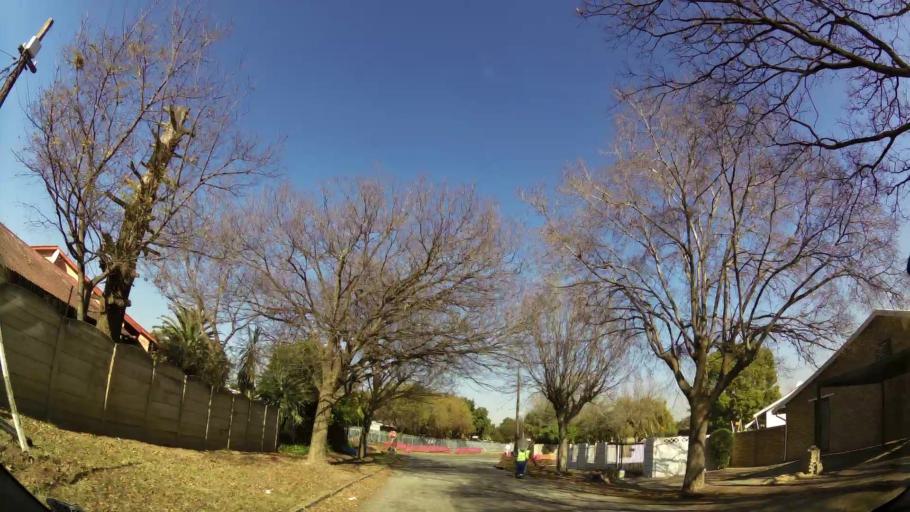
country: ZA
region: Gauteng
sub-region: Ekurhuleni Metropolitan Municipality
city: Benoni
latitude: -26.1511
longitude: 28.3046
